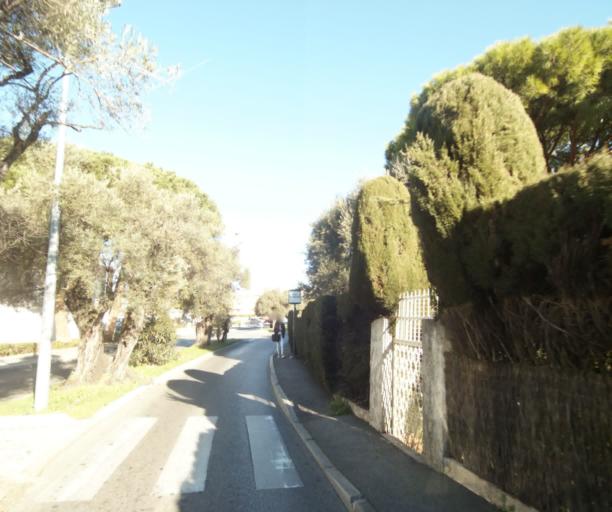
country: FR
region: Provence-Alpes-Cote d'Azur
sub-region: Departement des Alpes-Maritimes
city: Antibes
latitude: 43.5770
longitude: 7.1072
